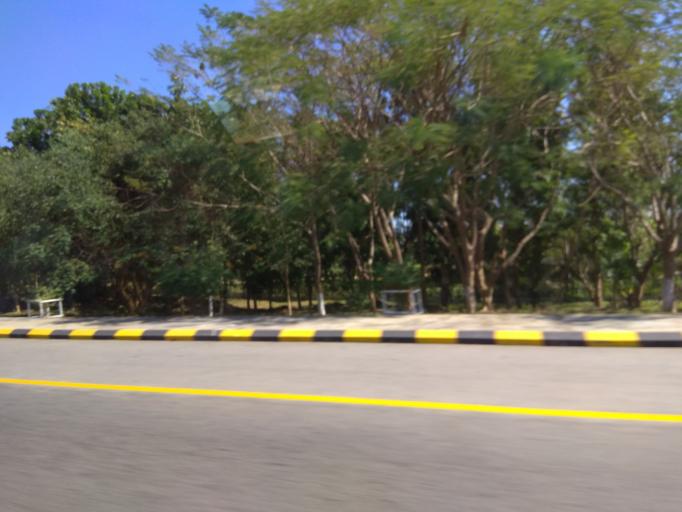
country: MM
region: Mandalay
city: Nay Pyi Taw
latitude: 19.7628
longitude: 96.1394
